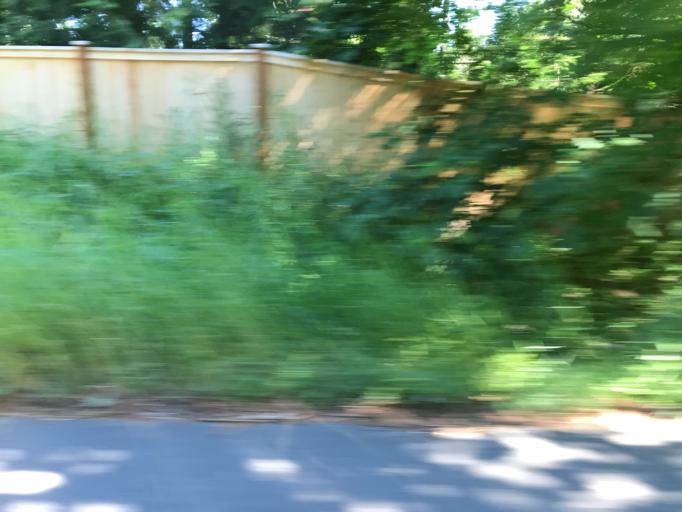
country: US
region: Washington
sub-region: King County
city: Redmond
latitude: 47.6460
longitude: -122.1483
